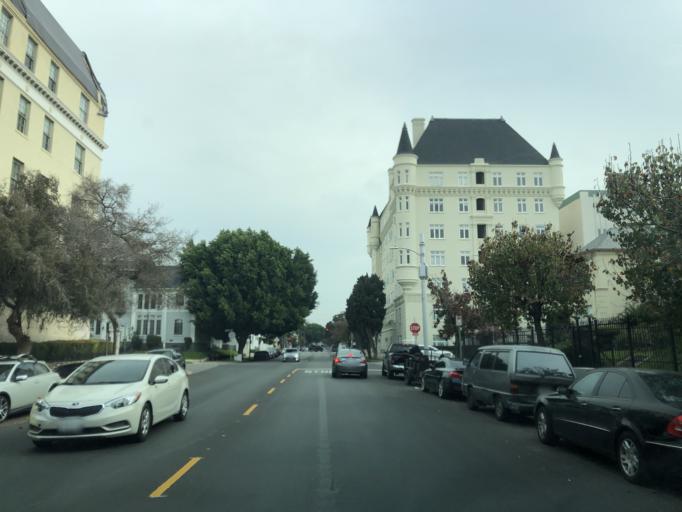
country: US
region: California
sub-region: Los Angeles County
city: Hollywood
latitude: 34.0558
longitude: -118.3074
